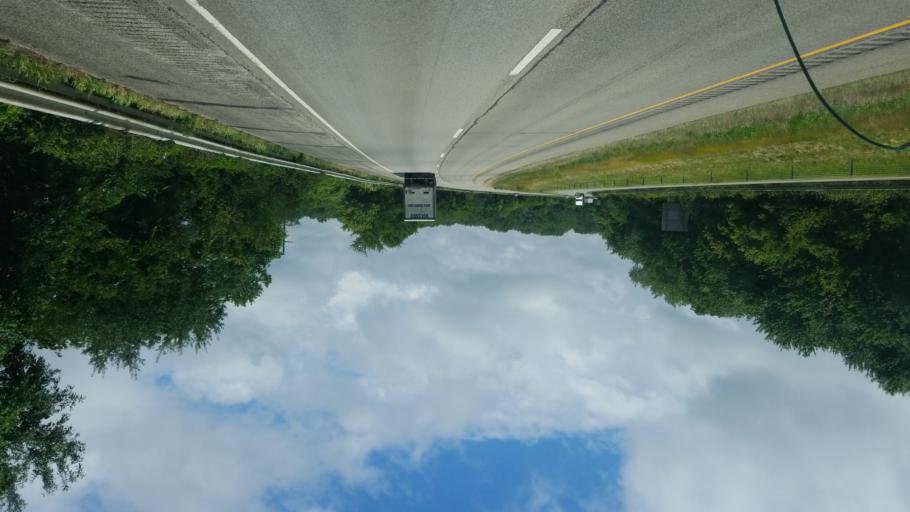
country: US
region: Indiana
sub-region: Vigo County
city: West Terre Haute
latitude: 39.4480
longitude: -87.4440
